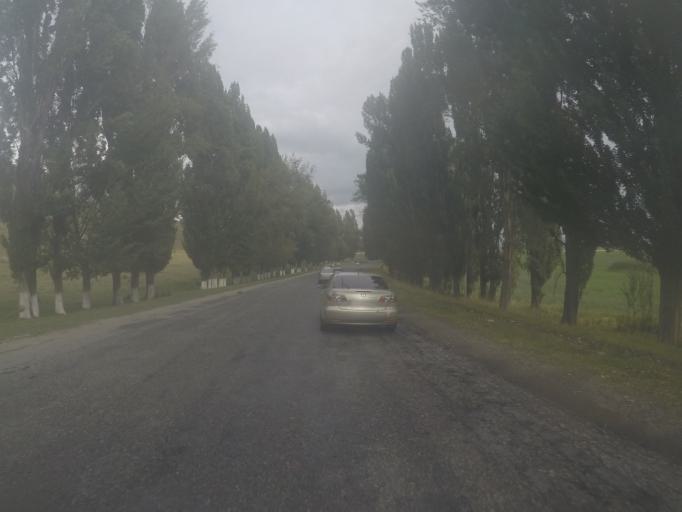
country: KG
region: Ysyk-Koel
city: Tyup
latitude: 42.7440
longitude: 78.0501
